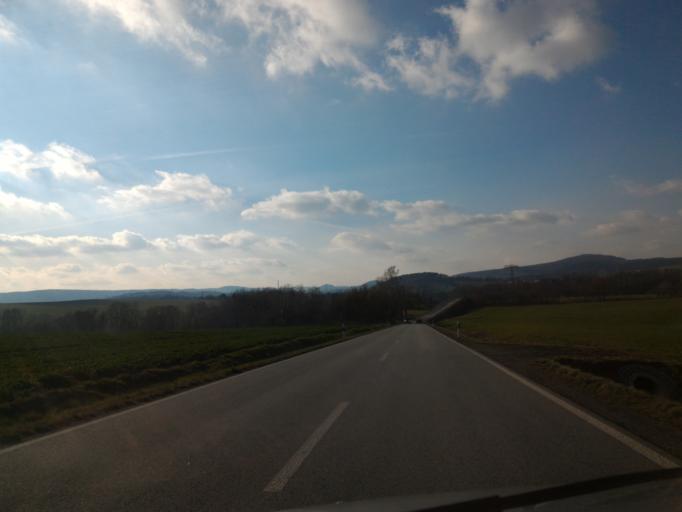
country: DE
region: Saxony
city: Grossschonau
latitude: 50.8883
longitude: 14.6929
